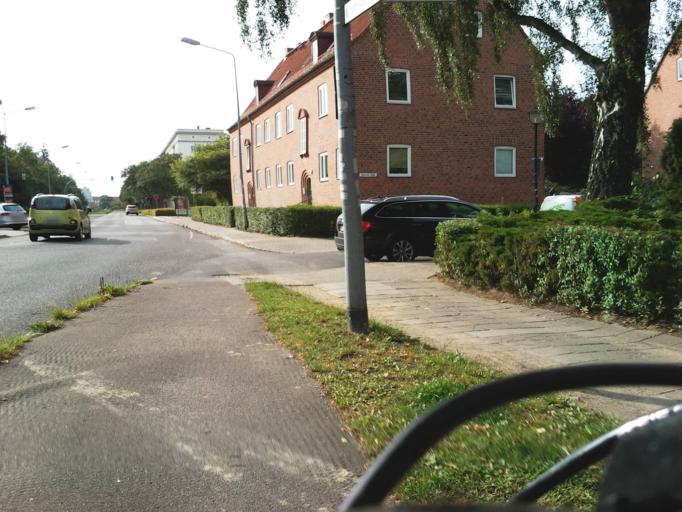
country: DE
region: Mecklenburg-Vorpommern
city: Kritzmow
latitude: 54.0965
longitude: 12.0817
